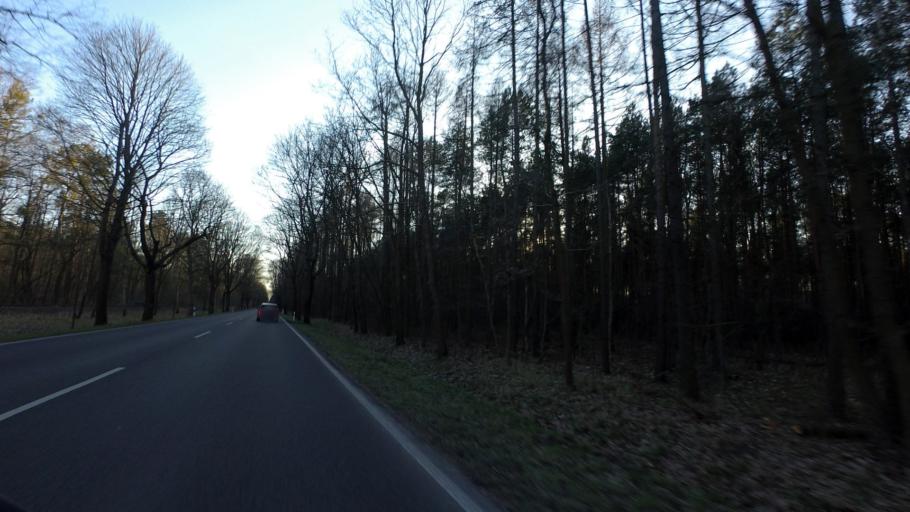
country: DE
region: Brandenburg
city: Werftpfuhl
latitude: 52.6691
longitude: 13.8132
